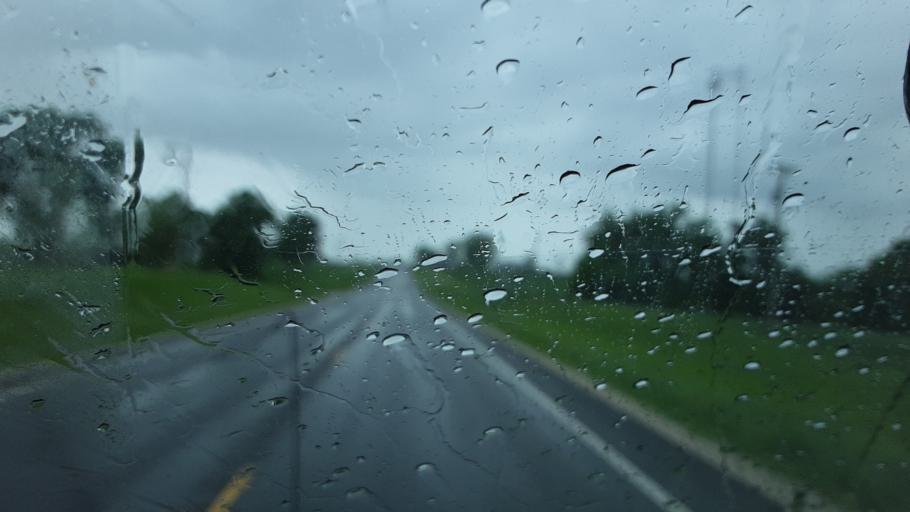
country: US
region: Missouri
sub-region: Monroe County
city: Paris
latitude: 39.4803
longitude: -92.1667
